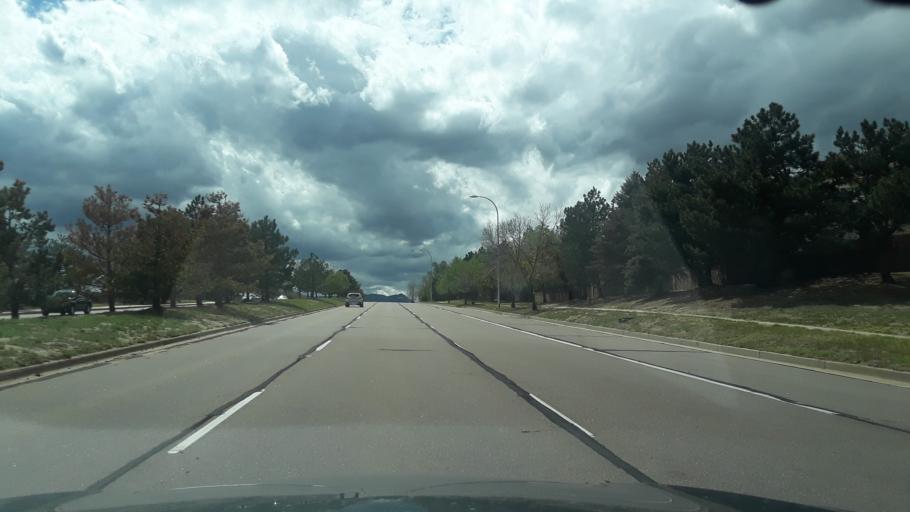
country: US
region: Colorado
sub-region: El Paso County
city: Black Forest
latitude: 38.9569
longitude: -104.7567
